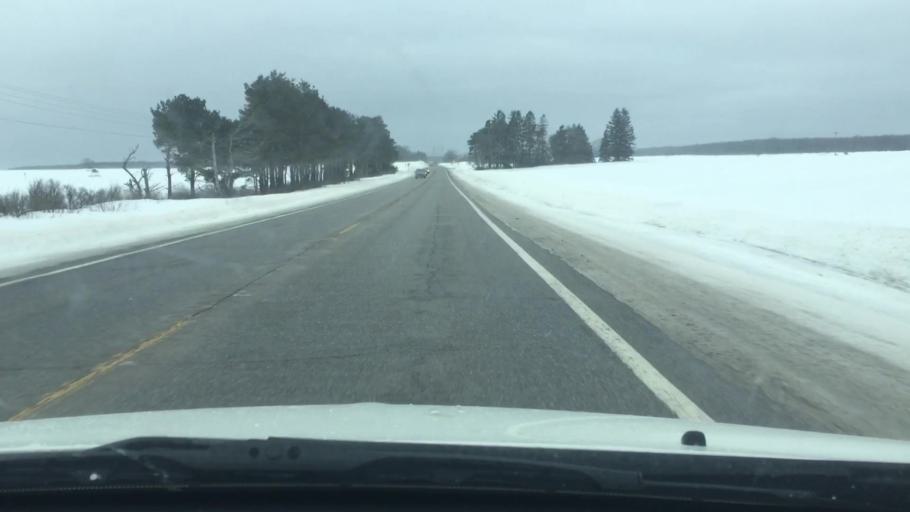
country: US
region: Michigan
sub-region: Otsego County
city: Gaylord
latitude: 45.0664
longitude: -84.8732
